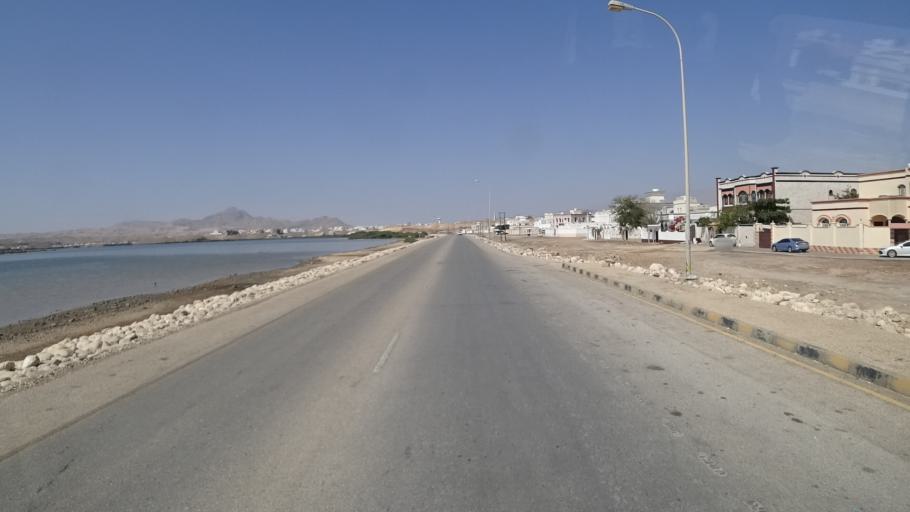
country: OM
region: Ash Sharqiyah
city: Sur
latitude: 22.5703
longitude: 59.5154
